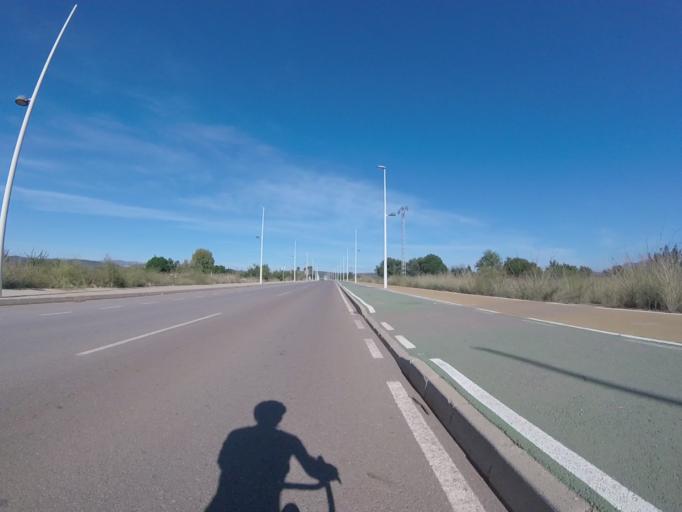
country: ES
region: Valencia
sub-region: Provincia de Castello
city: Torreblanca
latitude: 40.2111
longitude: 0.2242
